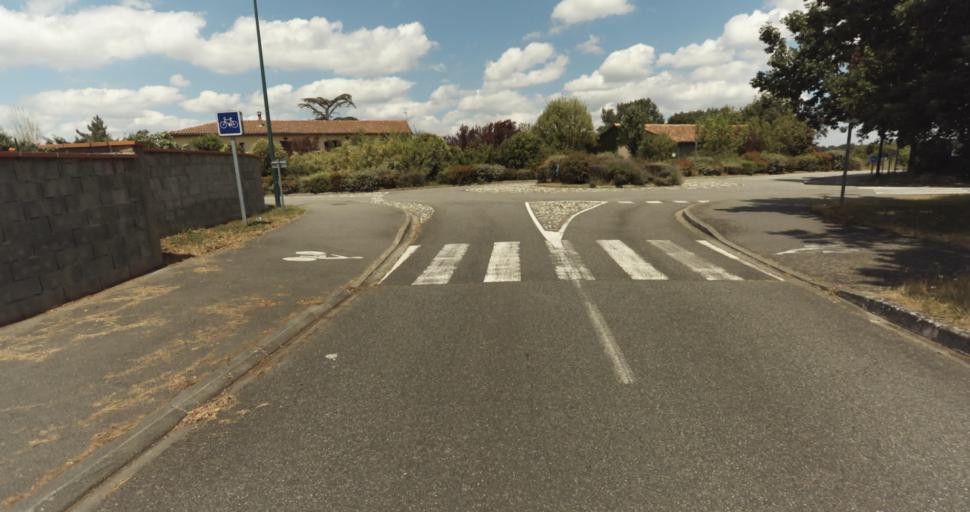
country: FR
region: Midi-Pyrenees
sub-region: Departement de la Haute-Garonne
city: Fontenilles
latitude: 43.5364
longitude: 1.1918
